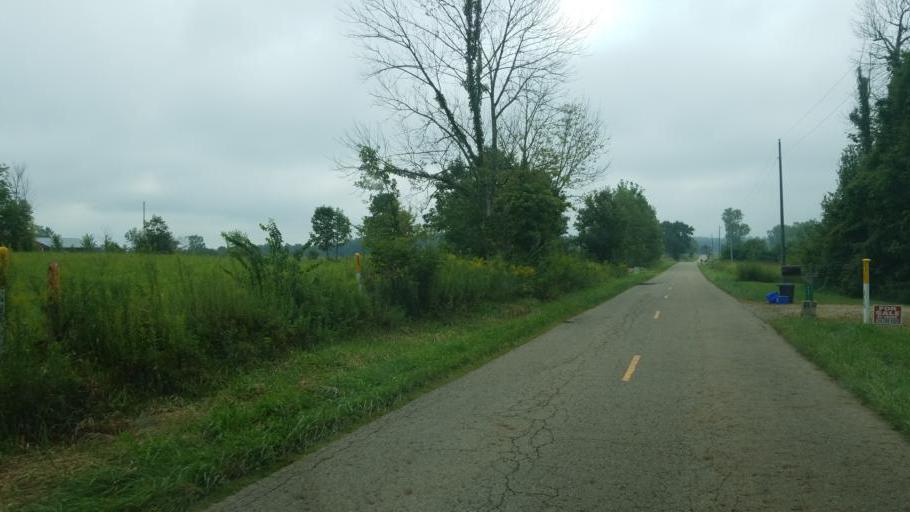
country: US
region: Ohio
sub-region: Licking County
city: Utica
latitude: 40.3095
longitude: -82.4524
